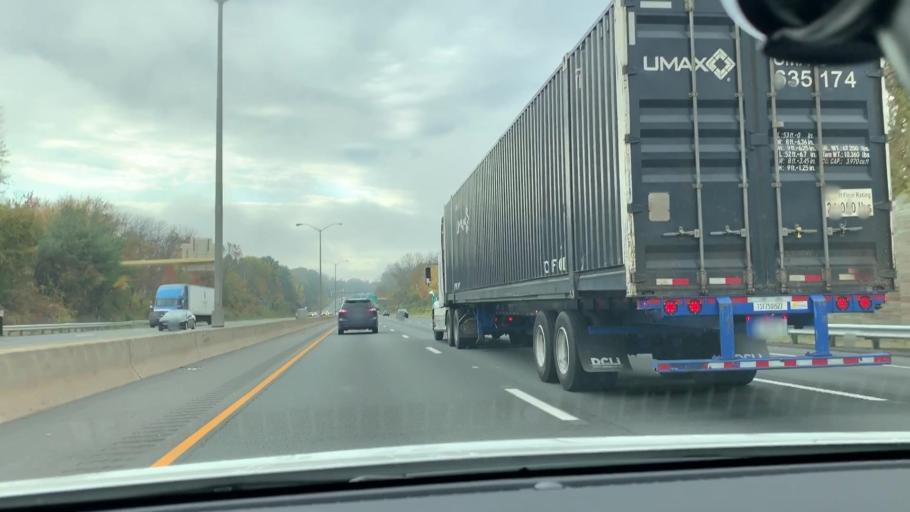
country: US
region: Connecticut
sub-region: Hartford County
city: Thompsonville
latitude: 42.0111
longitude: -72.5862
